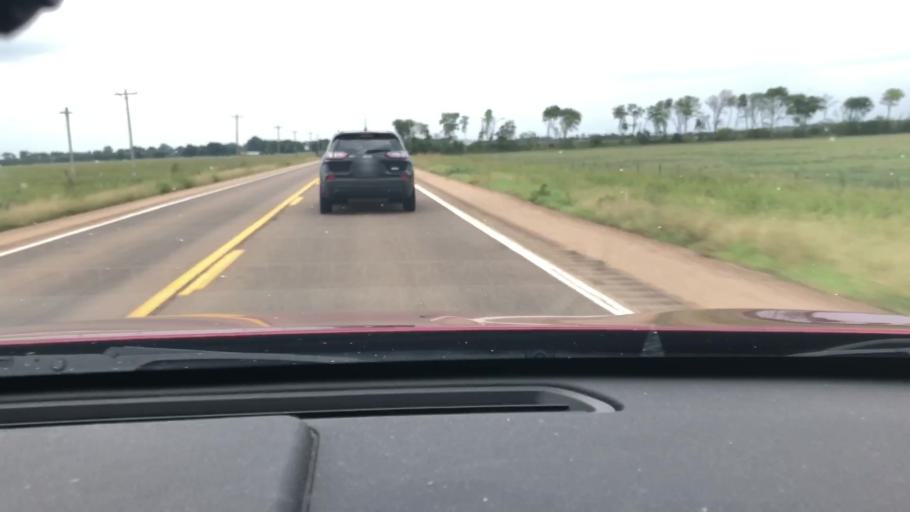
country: US
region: Arkansas
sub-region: Lafayette County
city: Lewisville
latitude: 33.3842
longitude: -93.7361
